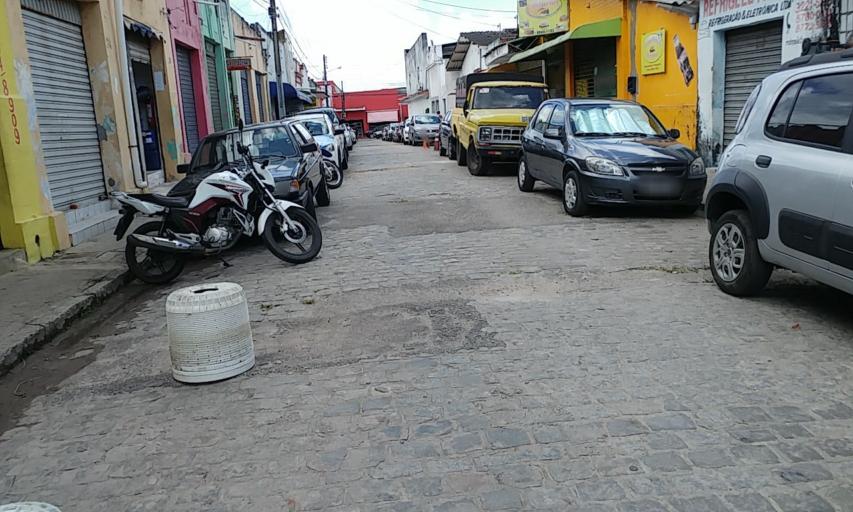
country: BR
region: Paraiba
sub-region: Joao Pessoa
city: Joao Pessoa
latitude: -7.1211
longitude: -34.8866
